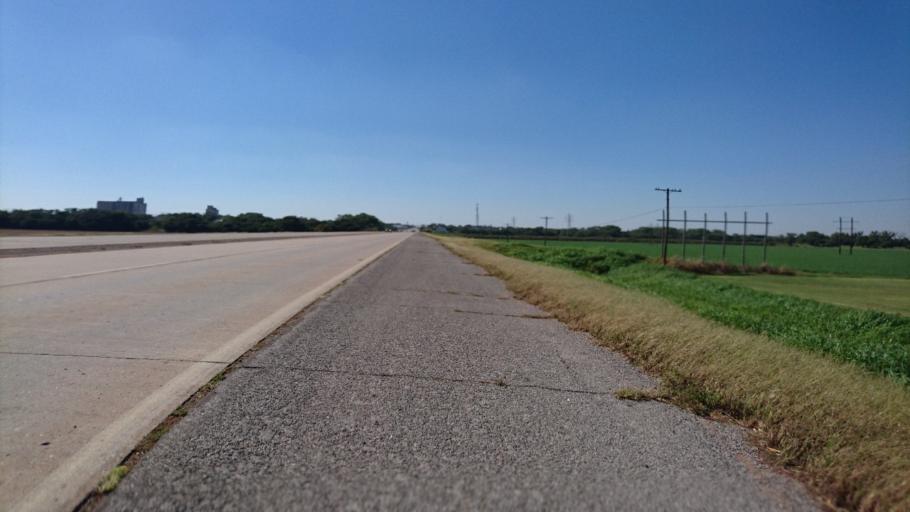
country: US
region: Oklahoma
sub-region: Custer County
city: Clinton
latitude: 35.5157
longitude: -98.9500
